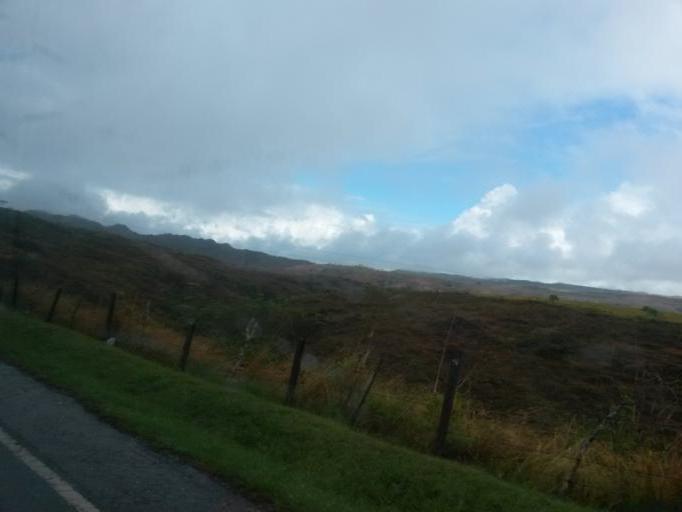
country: CO
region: Cauca
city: El Bordo
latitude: 2.1500
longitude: -76.9192
